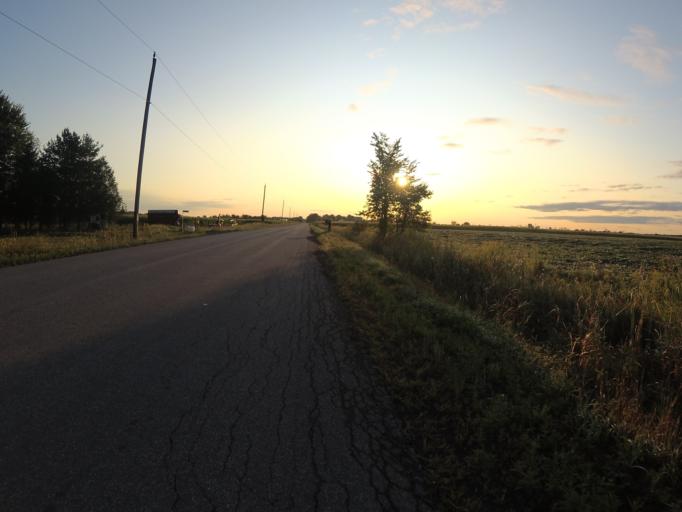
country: CA
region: Ontario
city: Ottawa
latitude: 45.1112
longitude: -75.5334
